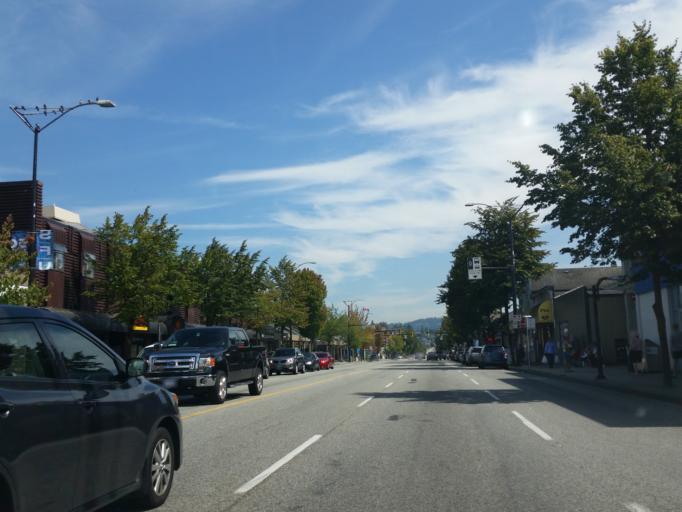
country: CA
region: British Columbia
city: Burnaby
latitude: 49.2810
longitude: -123.0142
